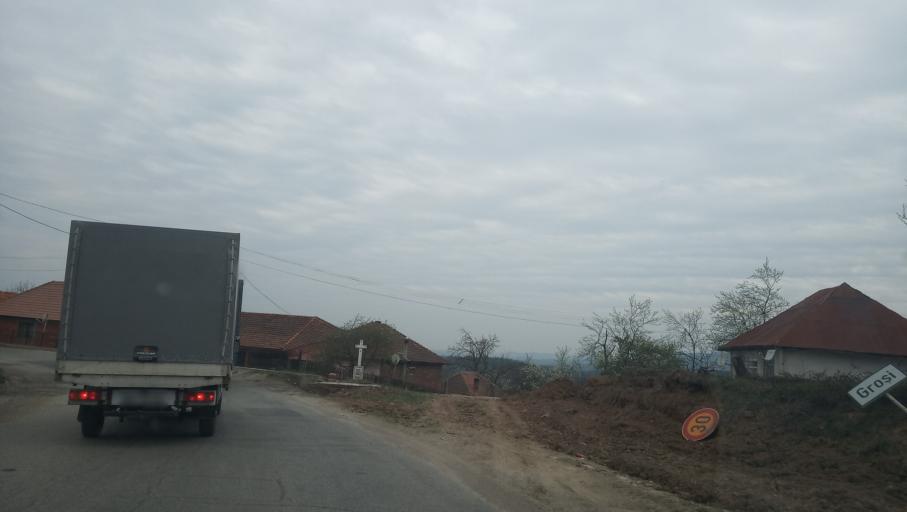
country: RO
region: Arad
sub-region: Comuna Varfurile
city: Varfurile
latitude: 46.3676
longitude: 22.5498
